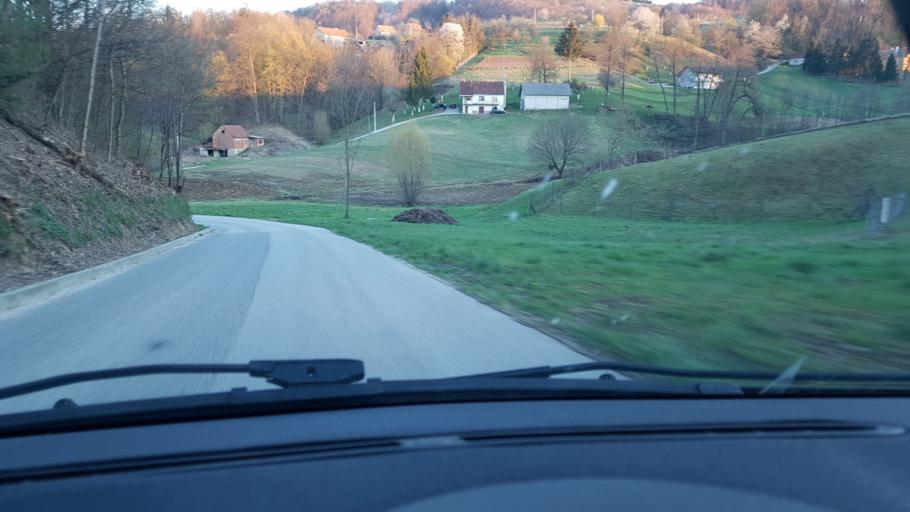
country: SI
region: Rogatec
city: Rogatec
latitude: 46.1936
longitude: 15.6861
